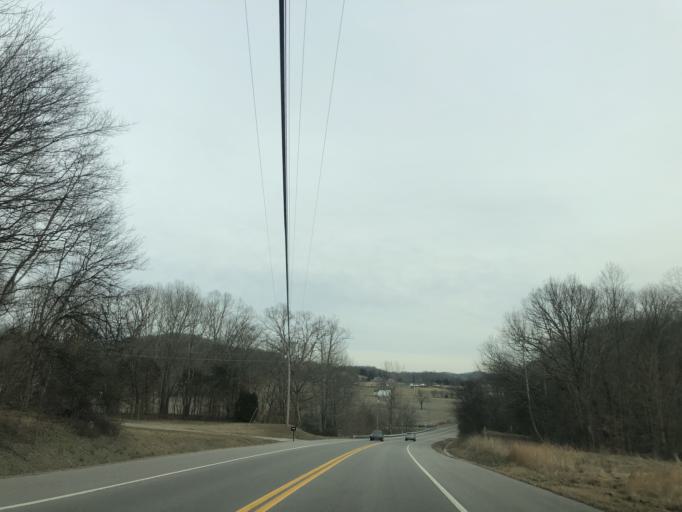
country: US
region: Tennessee
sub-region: Sumner County
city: White House
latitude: 36.4679
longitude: -86.5641
